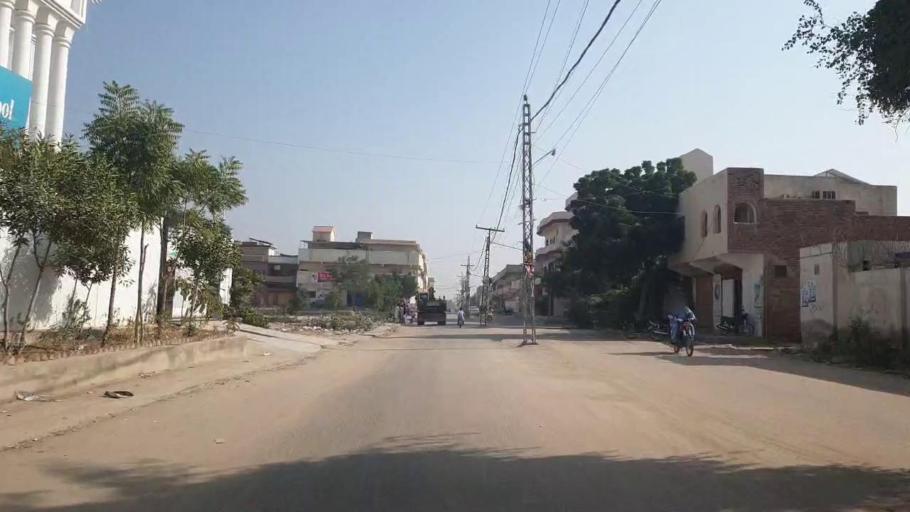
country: PK
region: Sindh
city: Jamshoro
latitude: 25.4124
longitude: 68.2748
